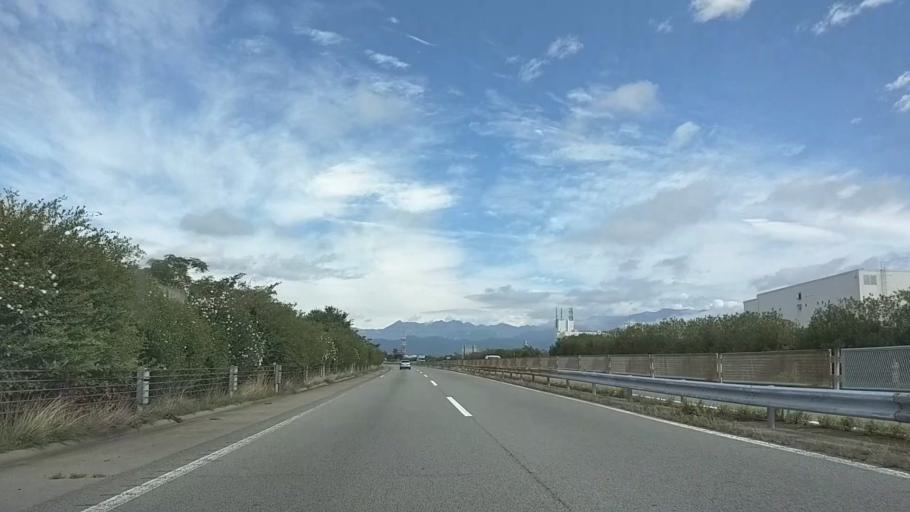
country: JP
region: Yamanashi
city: Kofu-shi
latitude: 35.6193
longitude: 138.5476
